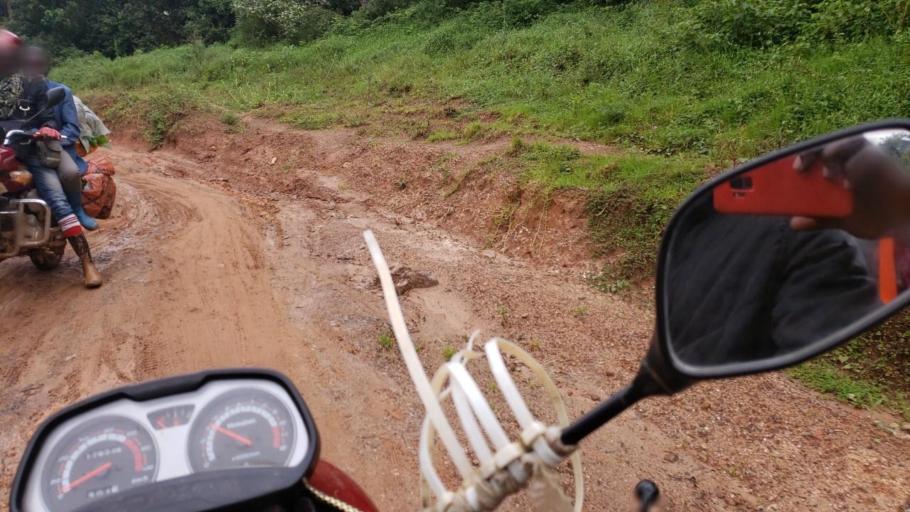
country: CD
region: South Kivu
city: Kabare
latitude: -2.2568
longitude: 28.6487
